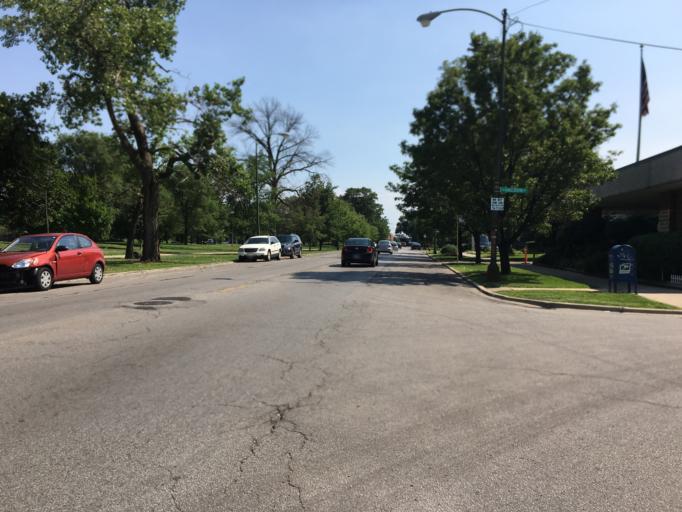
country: US
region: Illinois
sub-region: Cook County
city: Cicero
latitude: 41.9020
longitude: -87.7068
